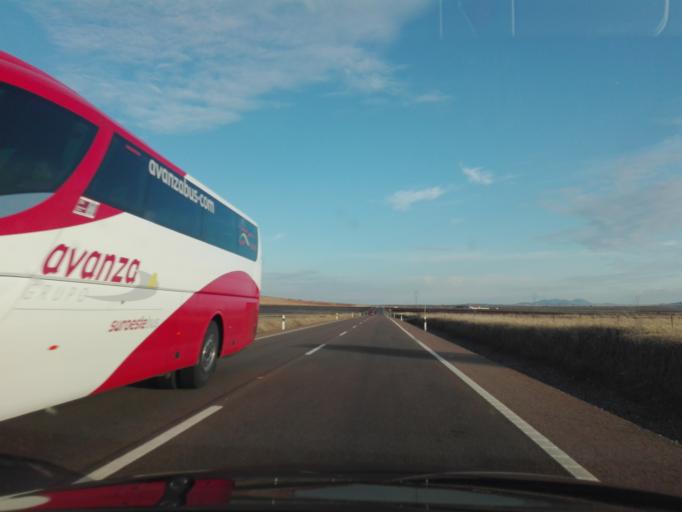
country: ES
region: Extremadura
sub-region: Provincia de Badajoz
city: Usagre
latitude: 38.3615
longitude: -6.2222
